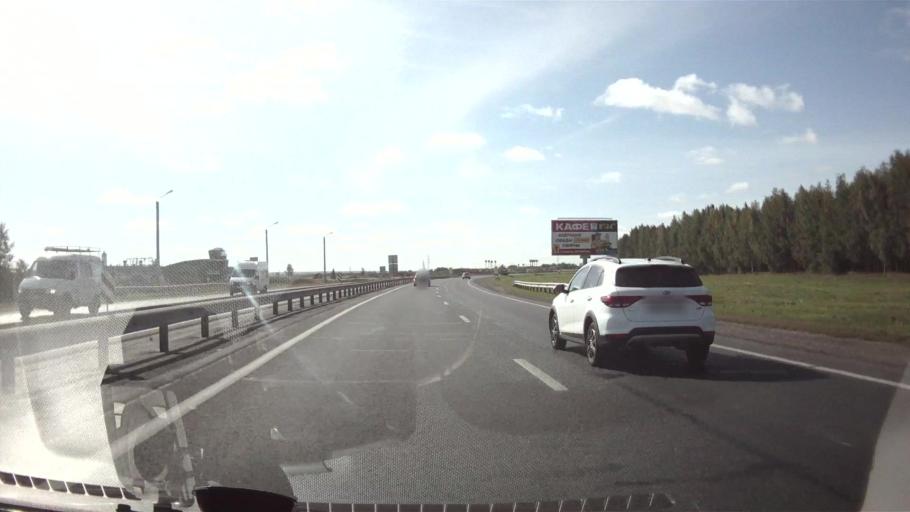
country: RU
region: Ulyanovsk
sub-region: Ulyanovskiy Rayon
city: Ulyanovsk
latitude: 54.2740
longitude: 48.2612
